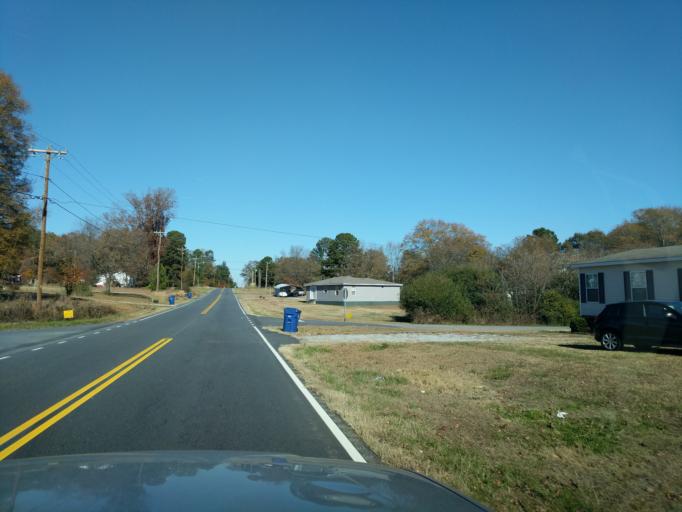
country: US
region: South Carolina
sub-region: Spartanburg County
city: Duncan
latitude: 34.9119
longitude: -82.1451
